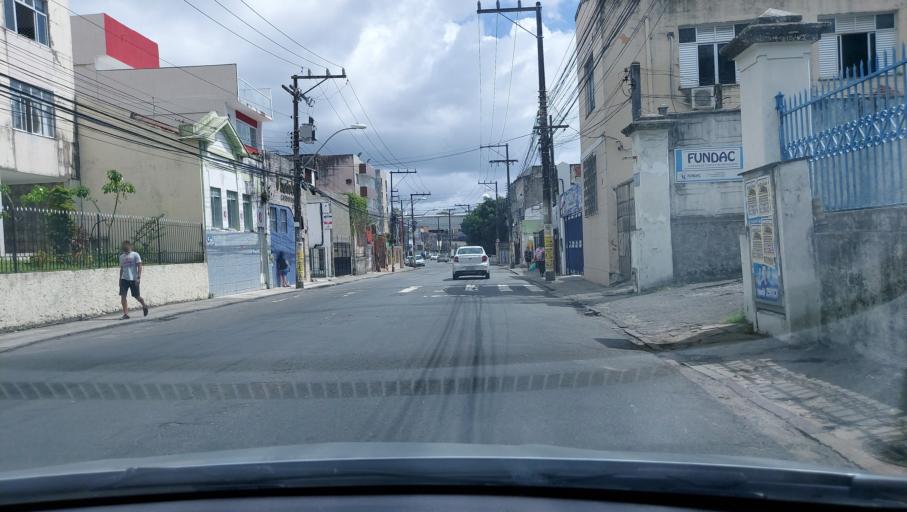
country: BR
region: Bahia
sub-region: Salvador
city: Salvador
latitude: -12.9785
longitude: -38.4976
